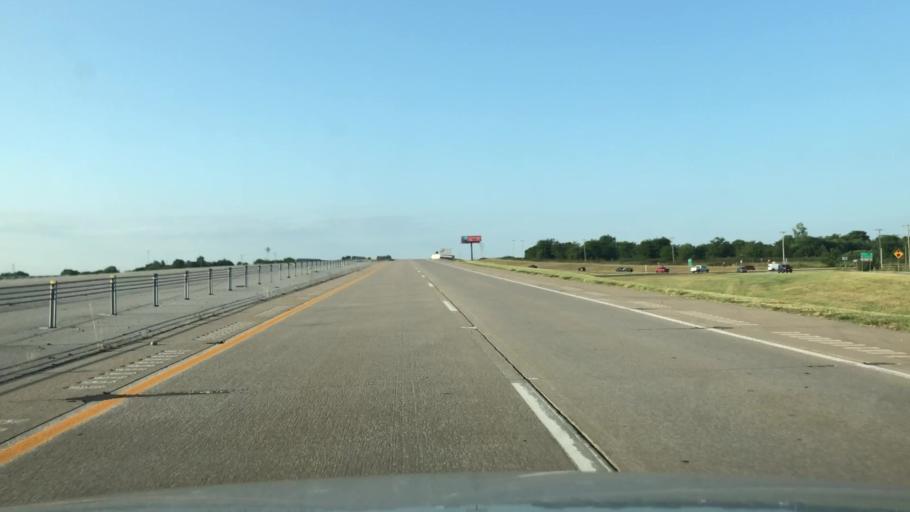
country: US
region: Oklahoma
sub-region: Osage County
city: Skiatook
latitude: 36.3677
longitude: -95.9208
